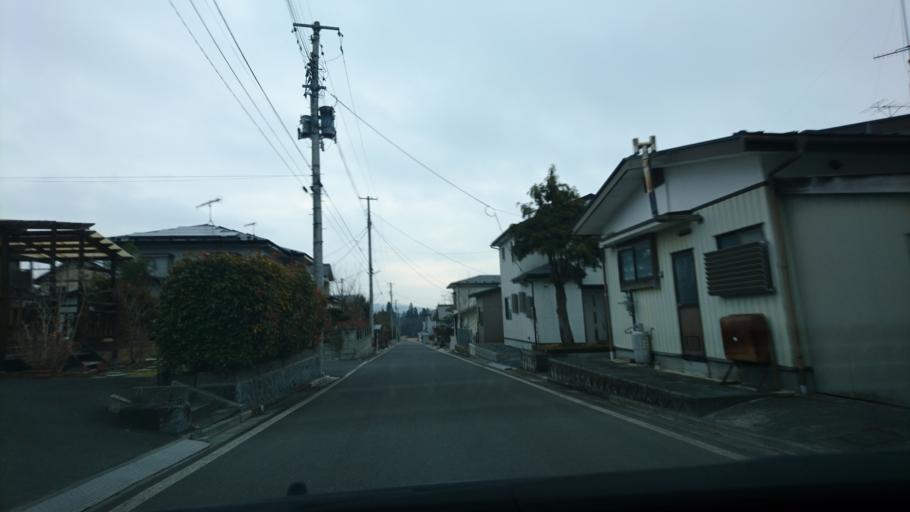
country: JP
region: Iwate
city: Ichinoseki
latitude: 38.9261
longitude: 141.3340
